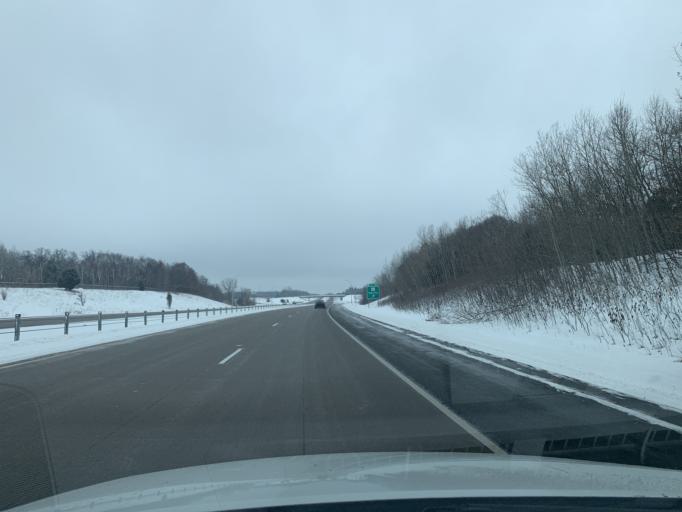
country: US
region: Minnesota
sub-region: Chisago County
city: Harris
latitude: 45.5840
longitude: -92.9932
